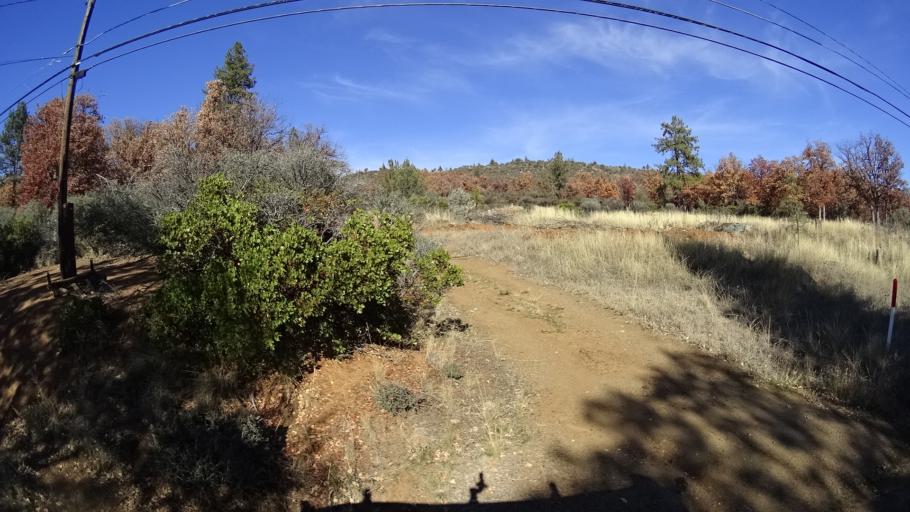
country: US
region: California
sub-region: Siskiyou County
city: Yreka
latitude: 41.7142
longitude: -122.6561
